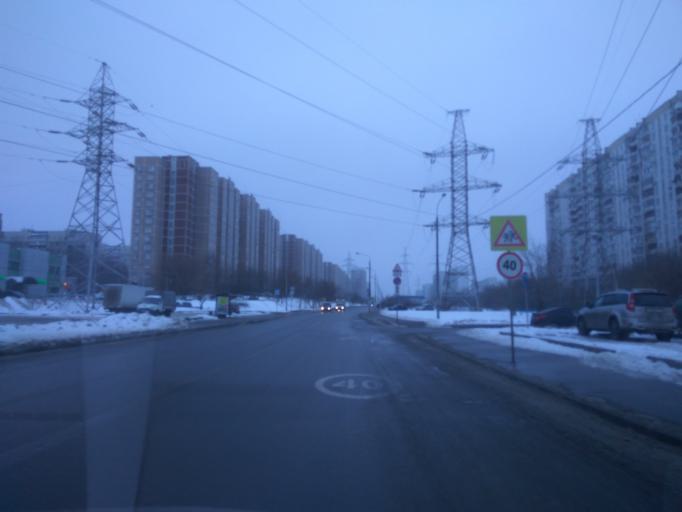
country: RU
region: Moscow
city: Orekhovo-Borisovo Severnoye
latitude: 55.6366
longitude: 37.6824
